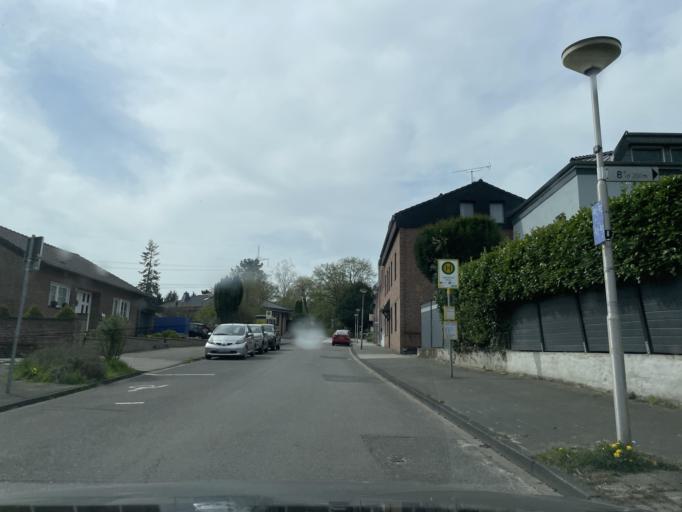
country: DE
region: North Rhine-Westphalia
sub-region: Regierungsbezirk Dusseldorf
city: Viersen
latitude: 51.2278
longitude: 6.4197
